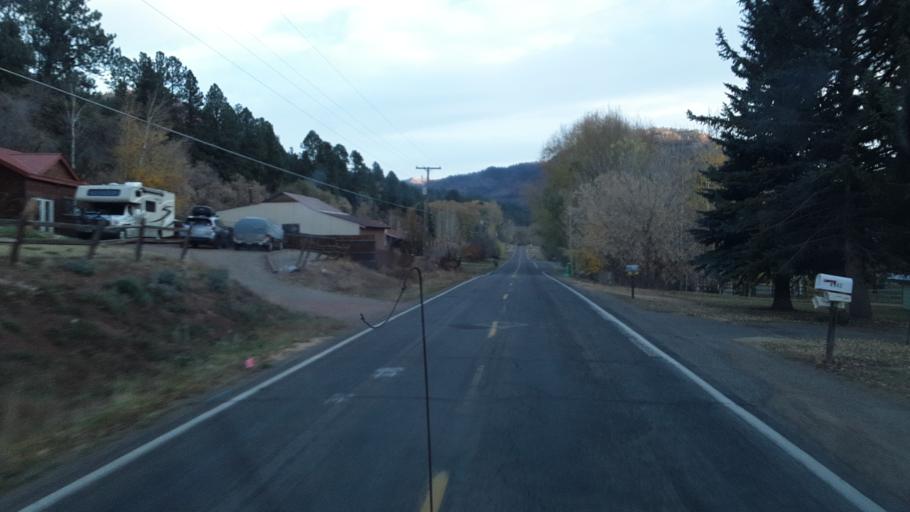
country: US
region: Colorado
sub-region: La Plata County
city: Durango
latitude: 37.3967
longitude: -107.8469
